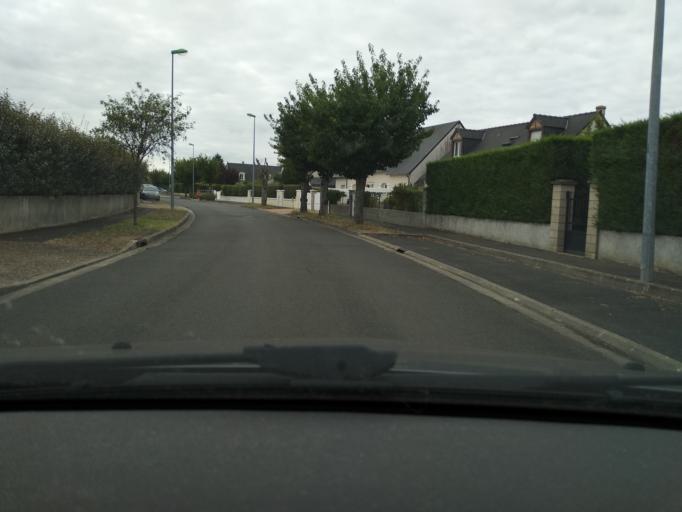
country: FR
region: Centre
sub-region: Departement d'Indre-et-Loire
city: Chanceaux-sur-Choisille
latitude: 47.4516
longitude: 0.7008
